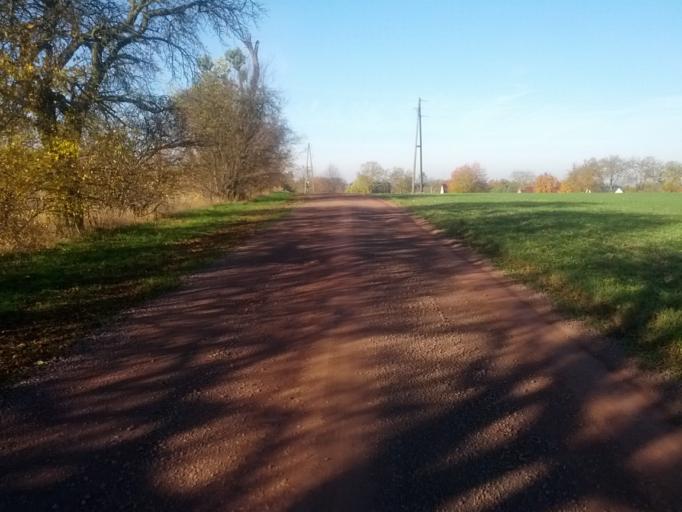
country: DE
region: Thuringia
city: Sonneborn
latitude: 50.9624
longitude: 10.5719
